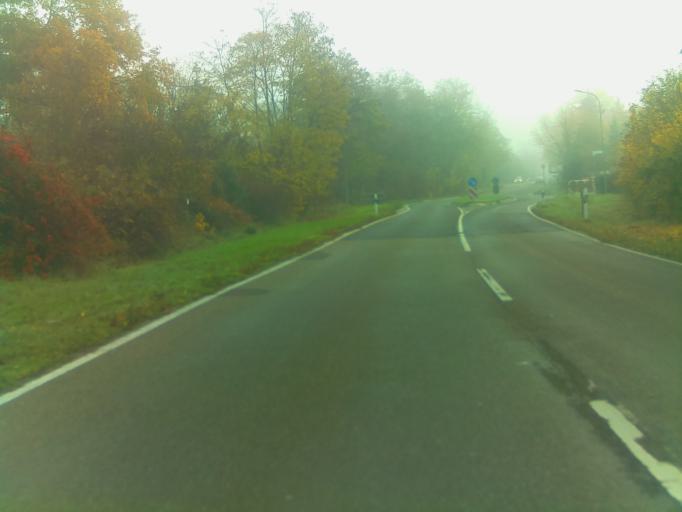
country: DE
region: Rheinland-Pfalz
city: Birkenheide
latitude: 49.4792
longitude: 8.2570
